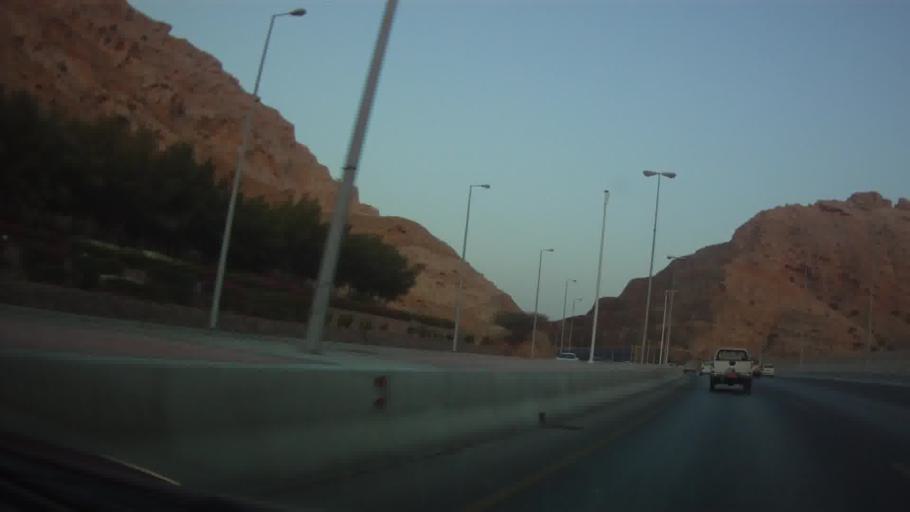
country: OM
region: Muhafazat Masqat
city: Muscat
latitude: 23.6156
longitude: 58.5271
